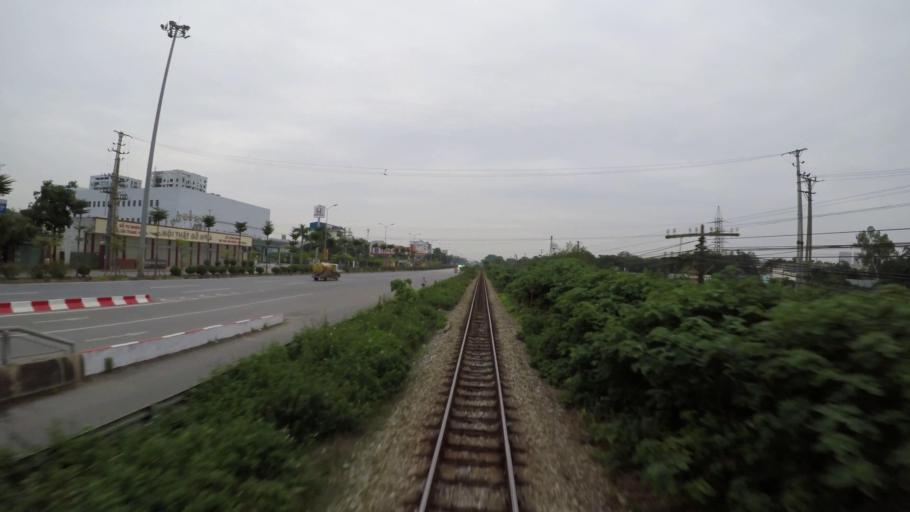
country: VN
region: Ha Noi
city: Trau Quy
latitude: 21.0062
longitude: 105.9587
